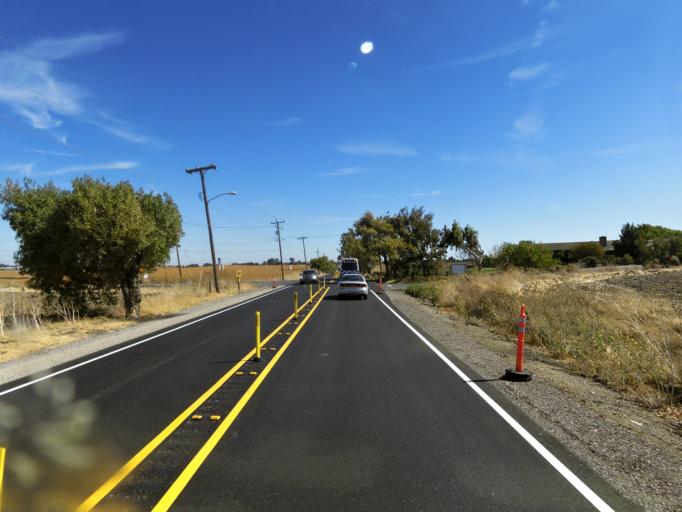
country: US
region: California
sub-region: Solano County
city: Rio Vista
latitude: 38.1710
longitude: -121.7099
